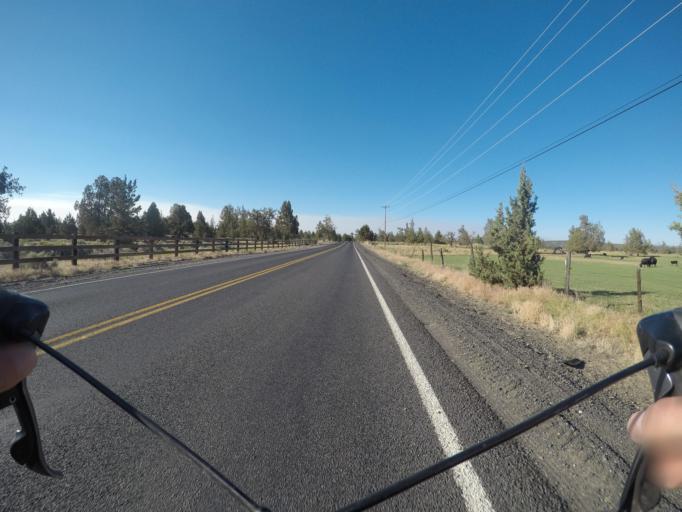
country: US
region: Oregon
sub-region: Deschutes County
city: Redmond
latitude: 44.2007
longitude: -121.2436
